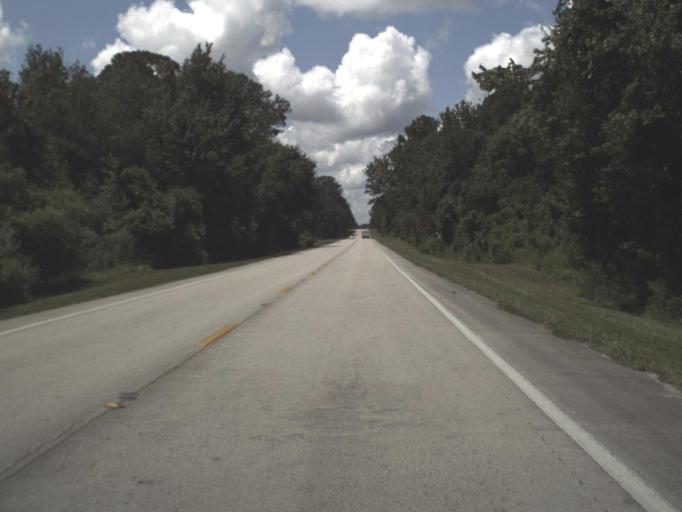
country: US
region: Florida
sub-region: Putnam County
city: Crescent City
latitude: 29.3823
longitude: -81.5088
